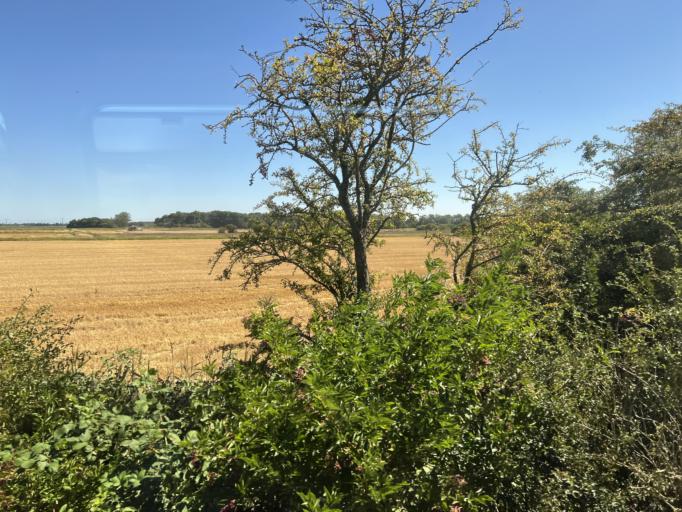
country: GB
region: England
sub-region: Lincolnshire
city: Spilsby
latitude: 53.1147
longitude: 0.1292
